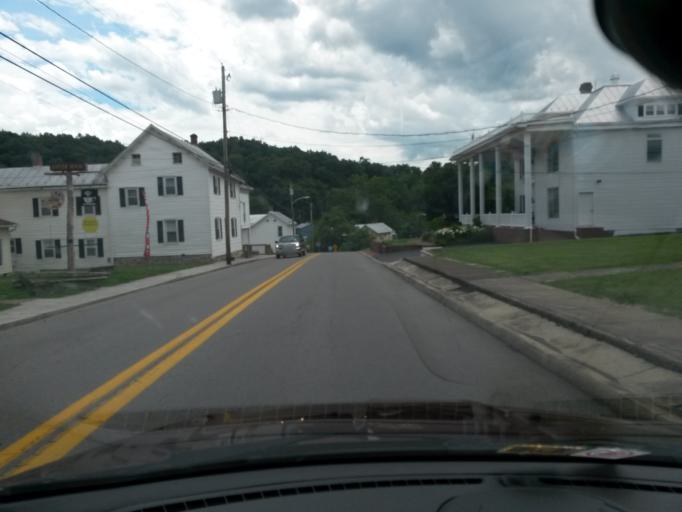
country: US
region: West Virginia
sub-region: Pendleton County
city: Franklin
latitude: 38.6413
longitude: -79.3314
